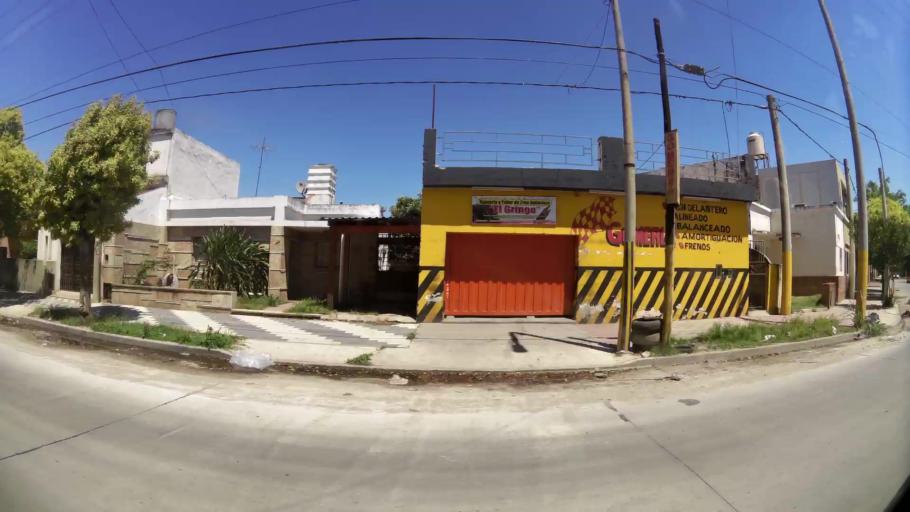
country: AR
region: Cordoba
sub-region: Departamento de Capital
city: Cordoba
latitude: -31.3835
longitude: -64.1509
